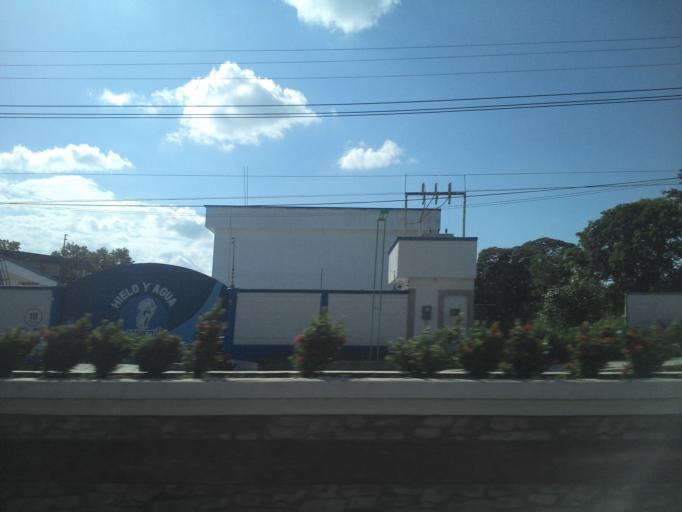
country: MX
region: Chiapas
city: Palenque
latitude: 17.5217
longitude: -91.9930
